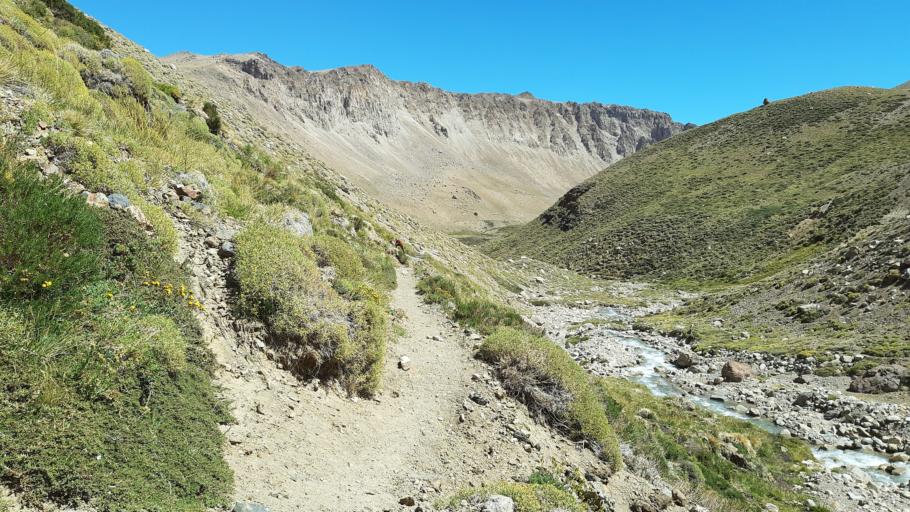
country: AR
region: Neuquen
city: Las Ovejas
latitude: -36.6789
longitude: -70.4940
